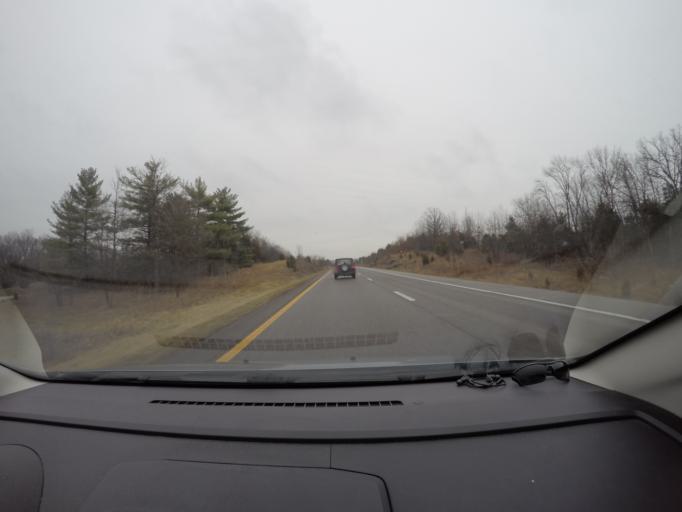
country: US
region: Missouri
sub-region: Montgomery County
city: Montgomery City
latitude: 38.8952
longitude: -91.6115
